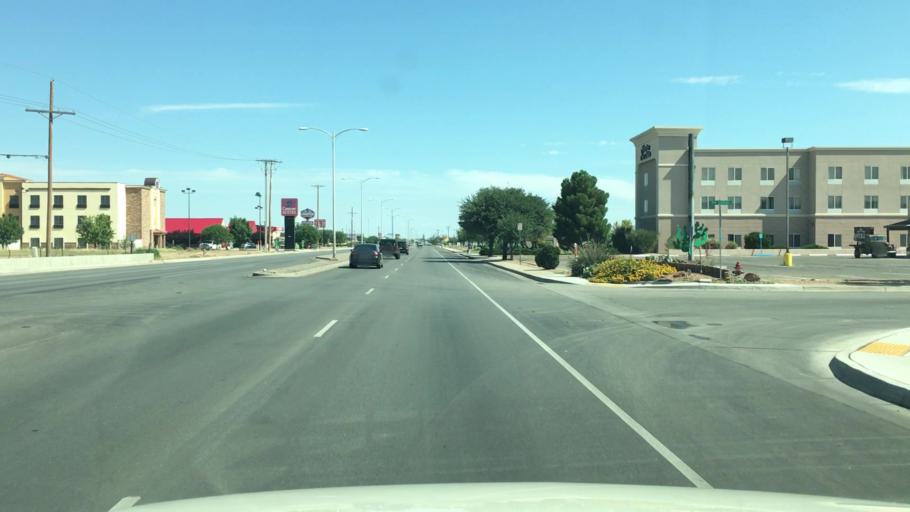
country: US
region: New Mexico
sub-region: Chaves County
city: Roswell
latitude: 33.4409
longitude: -104.5231
